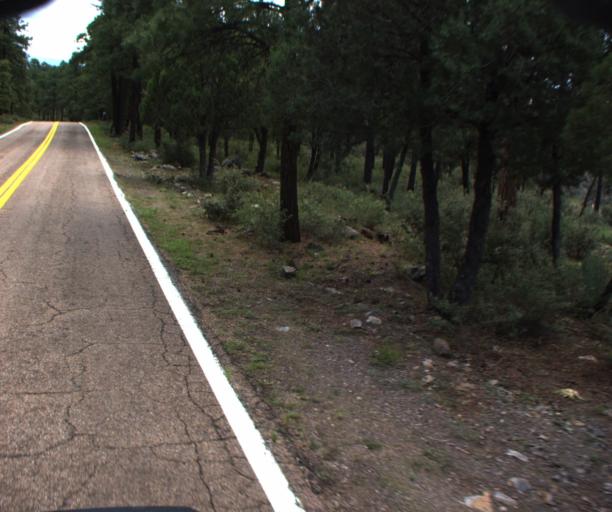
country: US
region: Arizona
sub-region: Greenlee County
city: Morenci
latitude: 33.5024
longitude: -109.3262
